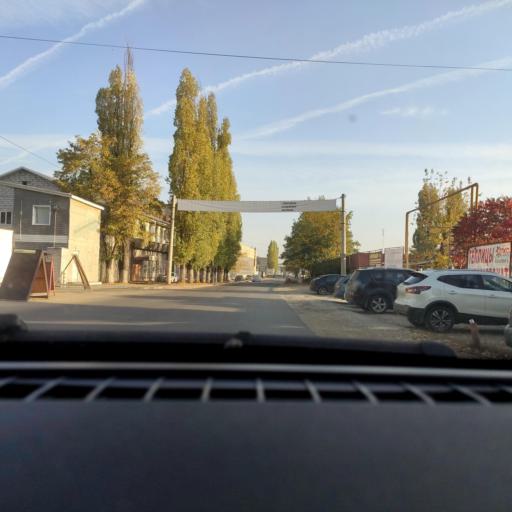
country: RU
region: Voronezj
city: Voronezh
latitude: 51.6530
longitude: 39.2819
